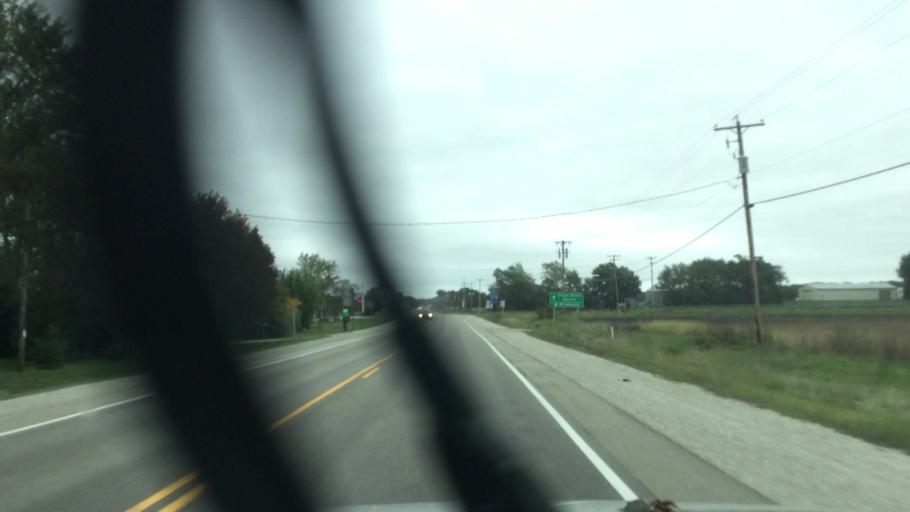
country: US
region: Wisconsin
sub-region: Racine County
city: Union Grove
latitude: 42.7422
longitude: -88.0744
